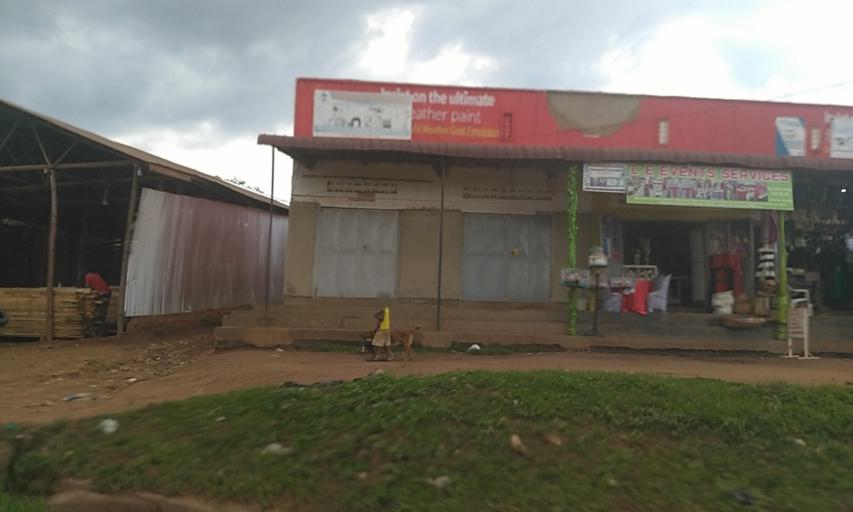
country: UG
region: Central Region
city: Kampala Central Division
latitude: 0.3240
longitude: 32.5032
